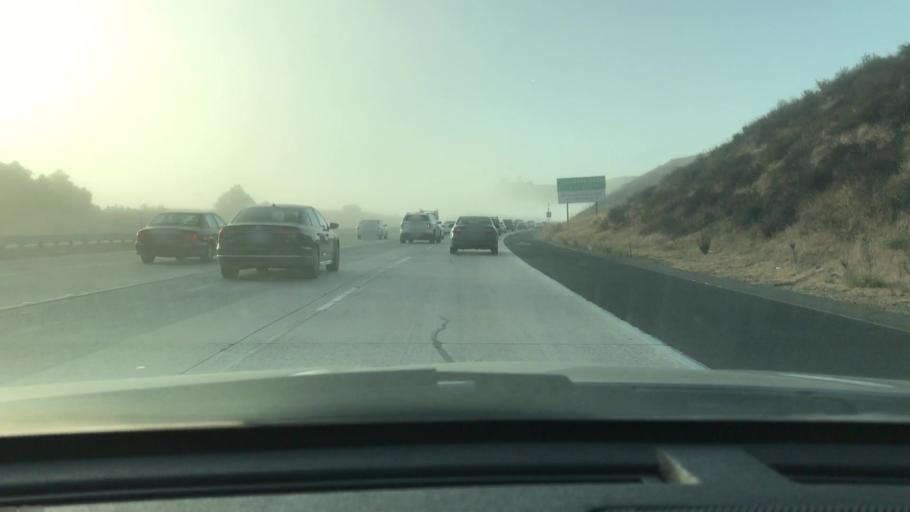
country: US
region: California
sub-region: Ventura County
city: Moorpark
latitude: 34.2574
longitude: -118.8417
